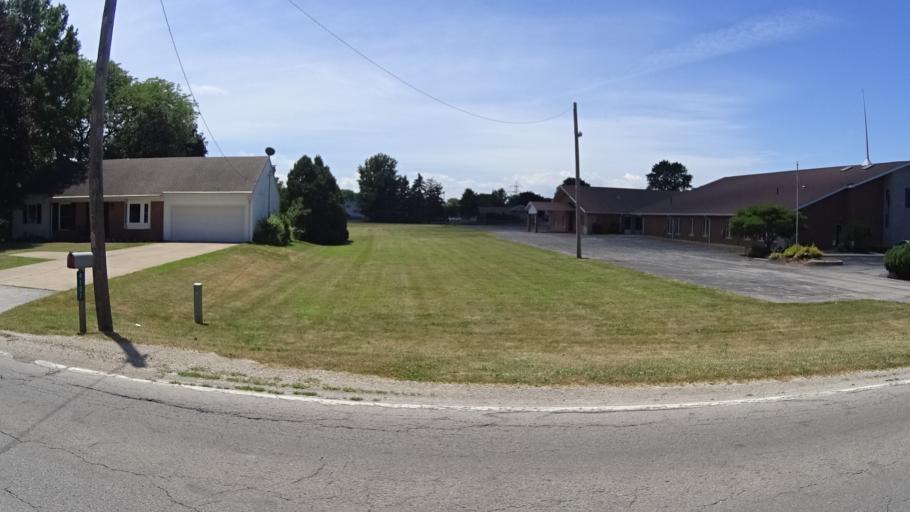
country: US
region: Ohio
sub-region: Erie County
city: Sandusky
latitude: 41.4105
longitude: -82.6842
